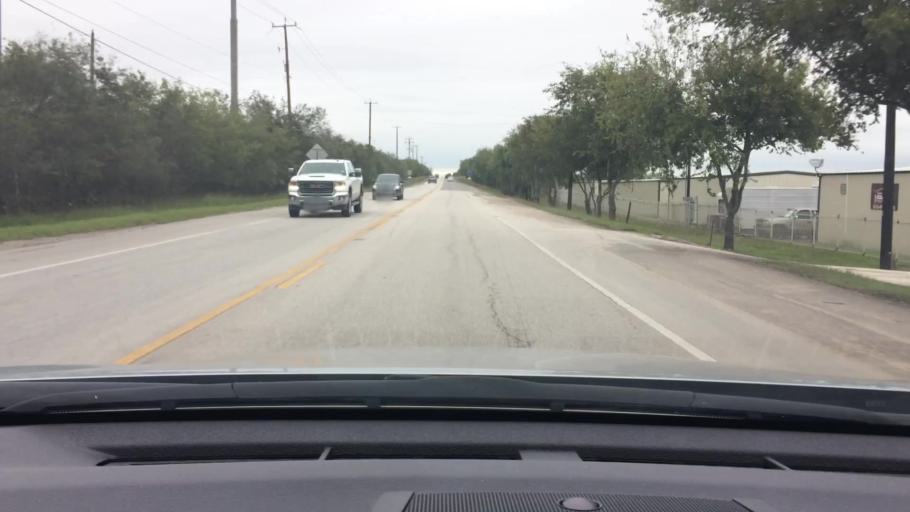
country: US
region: Texas
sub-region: Bexar County
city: Converse
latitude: 29.4798
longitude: -98.3134
